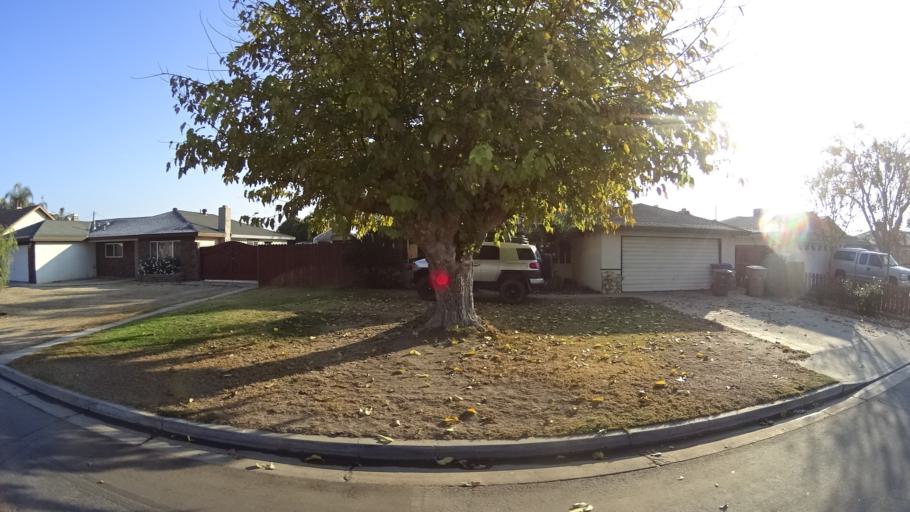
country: US
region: California
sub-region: Kern County
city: Greenfield
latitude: 35.2972
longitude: -119.0199
